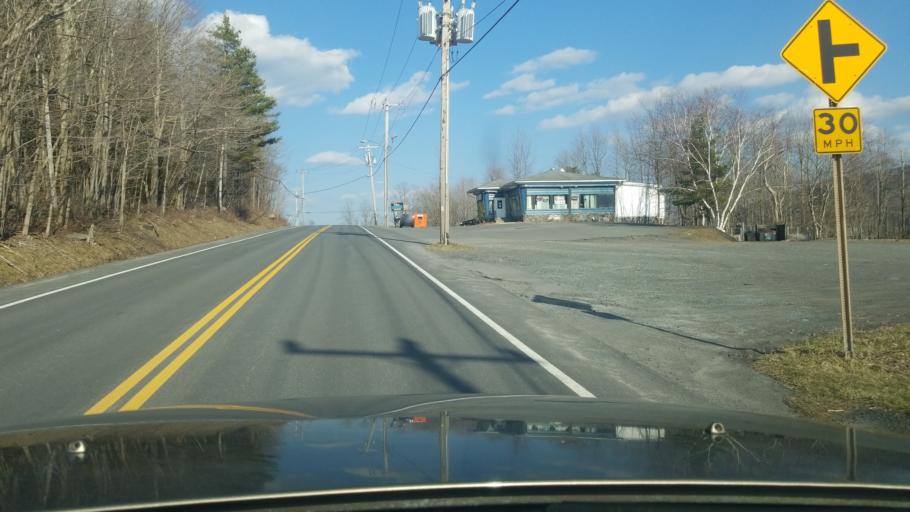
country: US
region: New York
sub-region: Ulster County
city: Manorville
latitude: 42.1958
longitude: -74.1193
